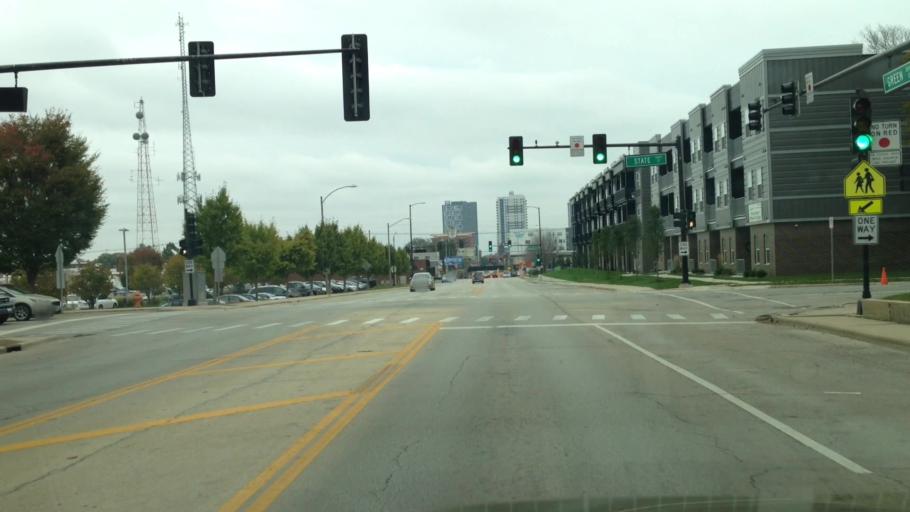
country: US
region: Illinois
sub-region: Champaign County
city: Champaign
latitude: 40.1101
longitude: -88.2472
